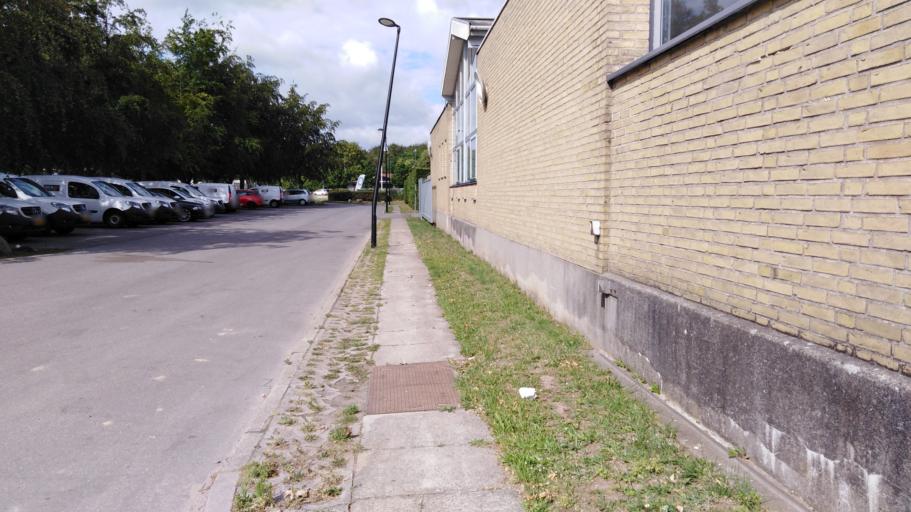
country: DK
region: Capital Region
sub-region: Albertslund Kommune
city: Albertslund
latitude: 55.6822
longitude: 12.3740
